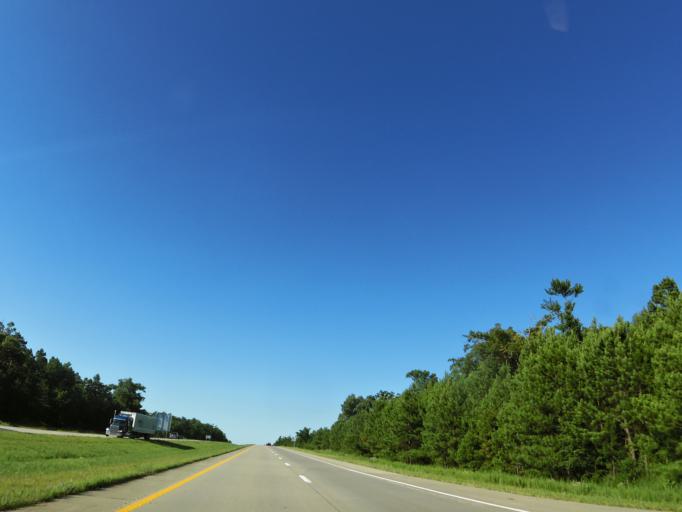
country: US
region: Missouri
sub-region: Butler County
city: Poplar Bluff
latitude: 36.7828
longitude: -90.4526
